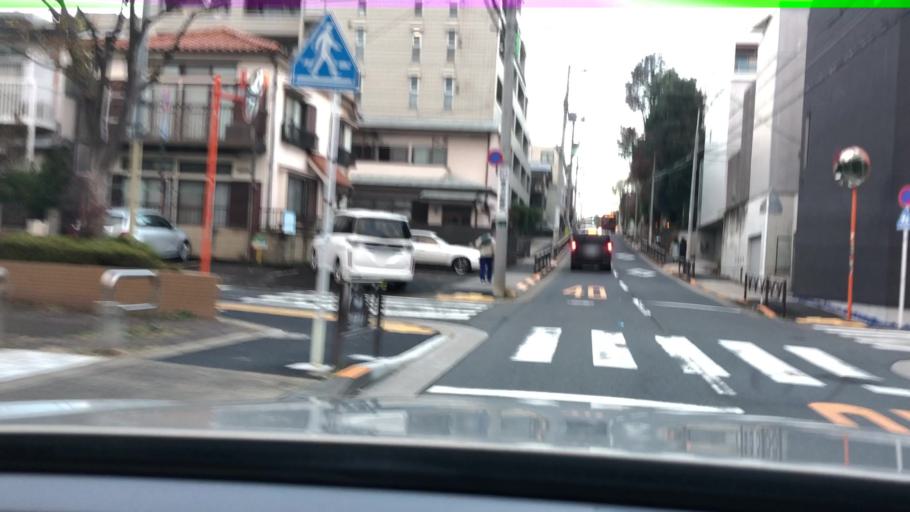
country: JP
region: Tokyo
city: Tokyo
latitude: 35.6119
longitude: 139.6596
